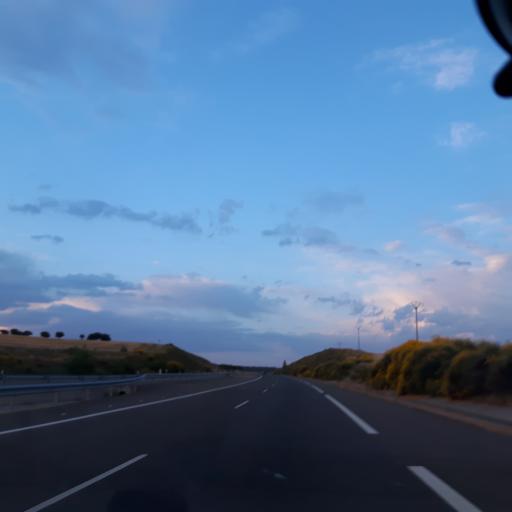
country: ES
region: Castille and Leon
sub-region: Provincia de Salamanca
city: Mozarbez
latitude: 40.8459
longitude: -5.6408
